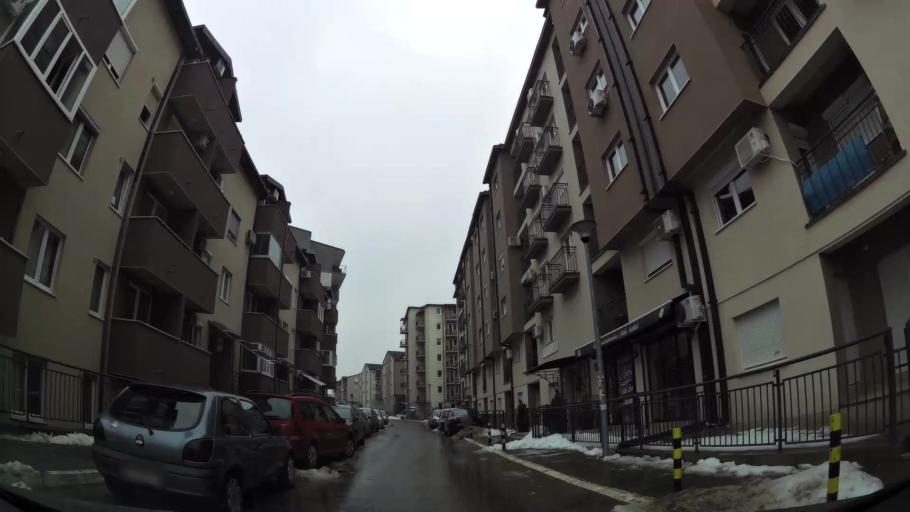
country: RS
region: Central Serbia
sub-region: Belgrade
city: Zvezdara
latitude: 44.7615
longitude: 20.5083
